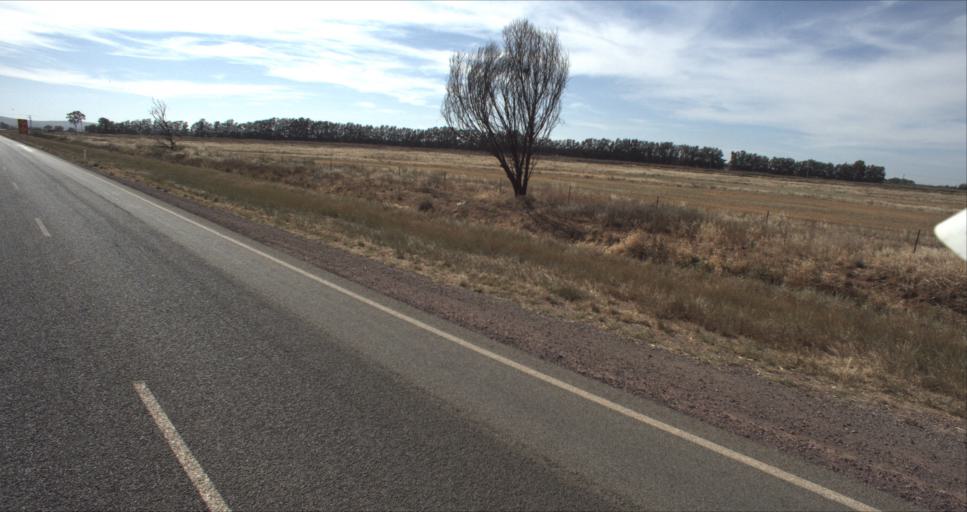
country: AU
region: New South Wales
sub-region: Leeton
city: Leeton
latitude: -34.5579
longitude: 146.4452
